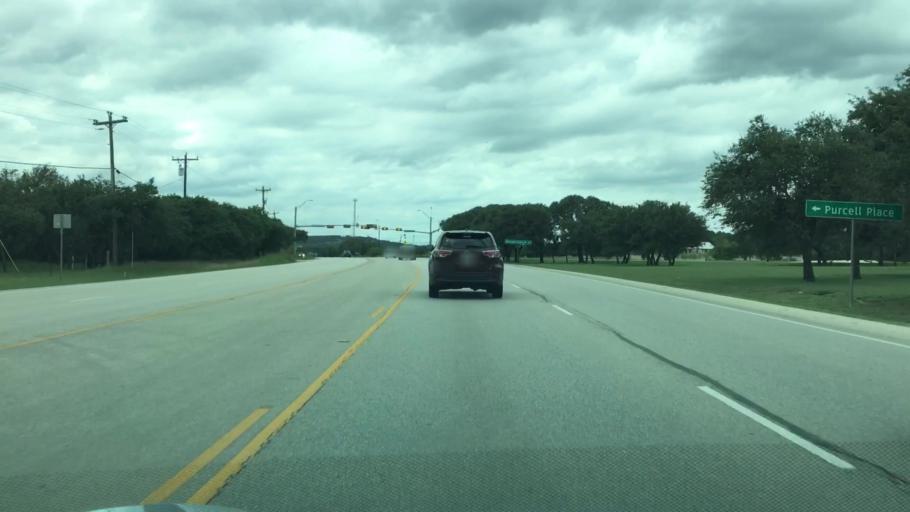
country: US
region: Texas
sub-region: Hays County
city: Dripping Springs
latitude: 30.2007
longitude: -98.1098
